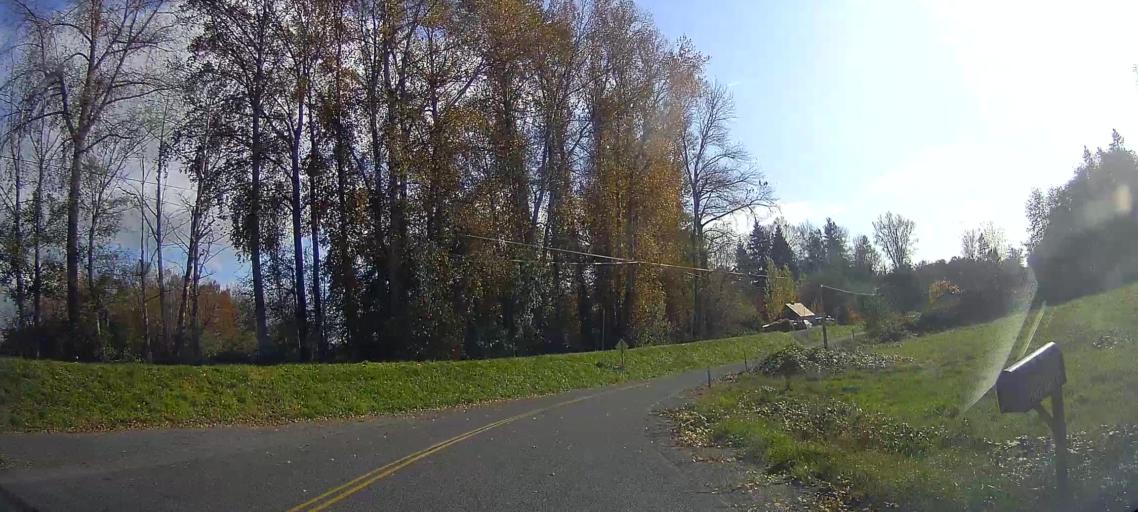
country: US
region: Washington
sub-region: Skagit County
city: Mount Vernon
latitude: 48.3407
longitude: -122.3523
